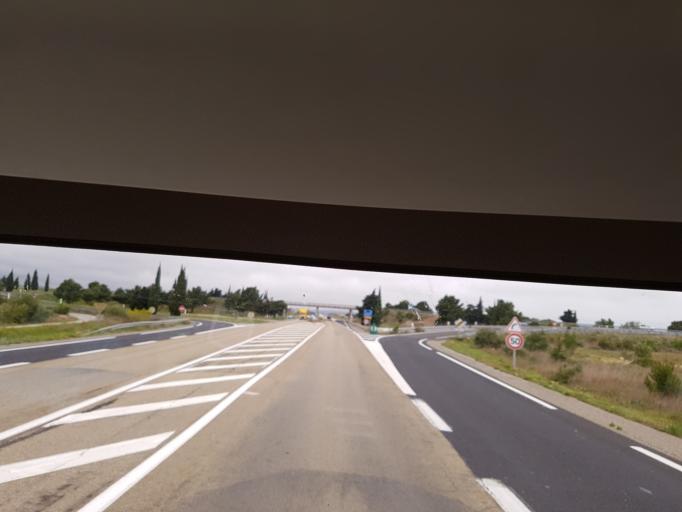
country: FR
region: Languedoc-Roussillon
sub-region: Departement de l'Aude
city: Leucate
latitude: 42.9346
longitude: 2.9918
